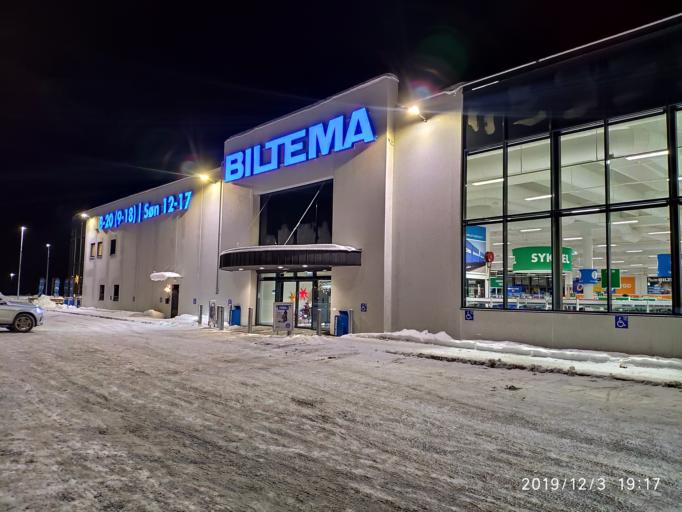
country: NO
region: Buskerud
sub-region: Gol
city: Gol
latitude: 60.6980
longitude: 8.9524
